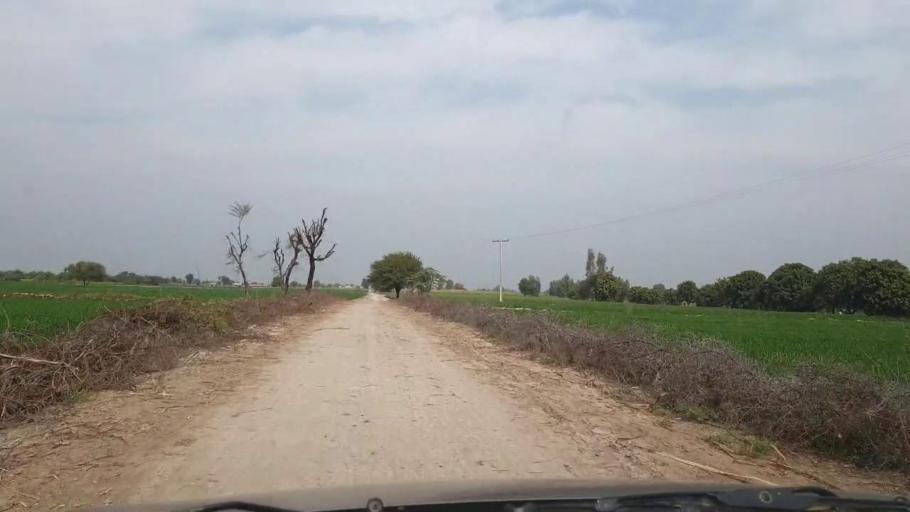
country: PK
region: Sindh
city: Sinjhoro
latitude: 26.0753
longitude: 68.8284
